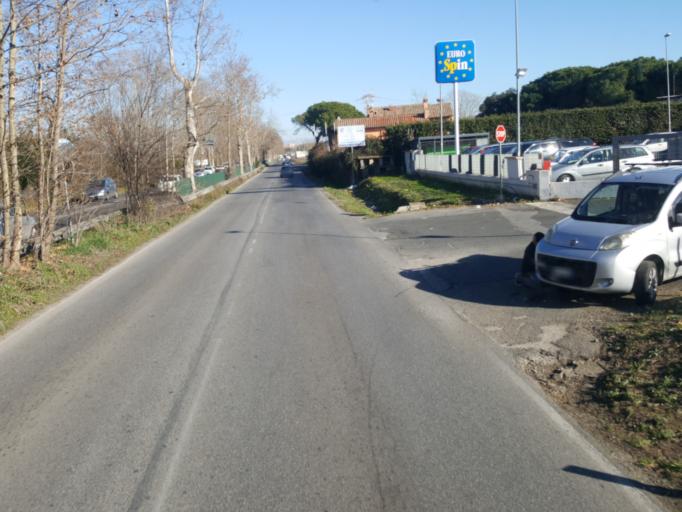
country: IT
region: Latium
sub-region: Citta metropolitana di Roma Capitale
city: Vitinia
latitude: 41.7923
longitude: 12.3871
